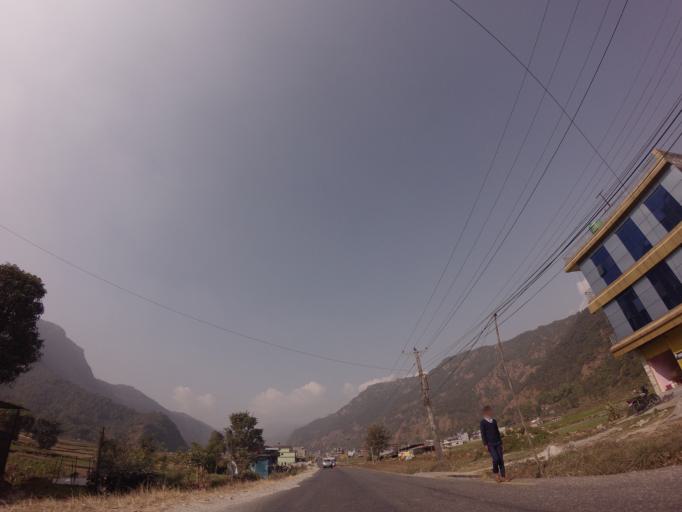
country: NP
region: Western Region
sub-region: Gandaki Zone
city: Pokhara
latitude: 28.2817
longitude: 83.9266
